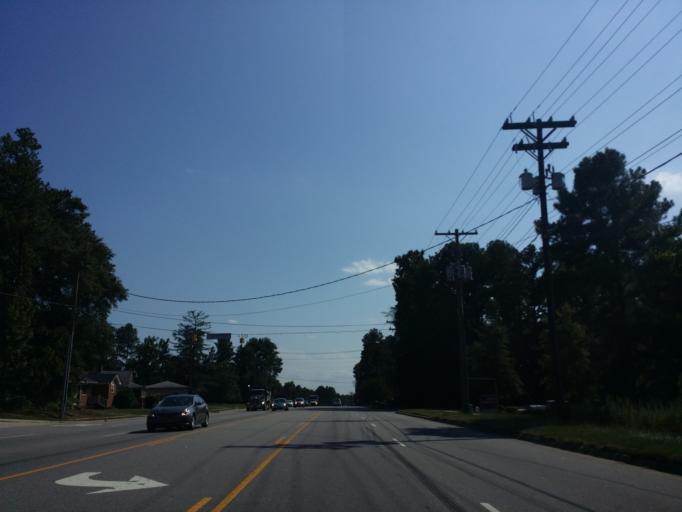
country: US
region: North Carolina
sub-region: Durham County
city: Durham
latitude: 35.9283
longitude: -78.8447
